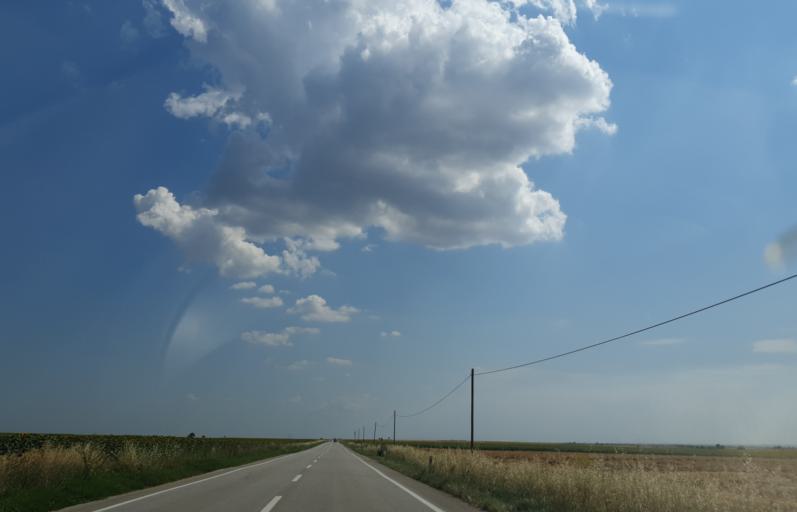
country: TR
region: Kirklareli
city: Buyukkaristiran
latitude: 41.4208
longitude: 27.5798
